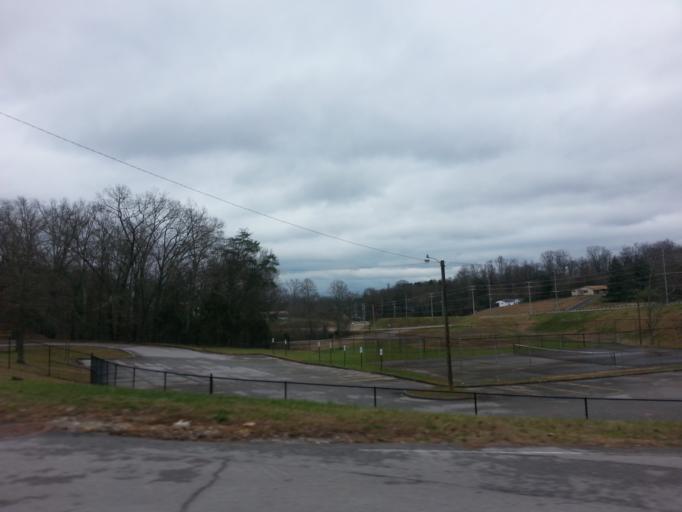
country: US
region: Tennessee
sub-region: Knox County
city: Knoxville
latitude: 35.9865
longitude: -84.0320
